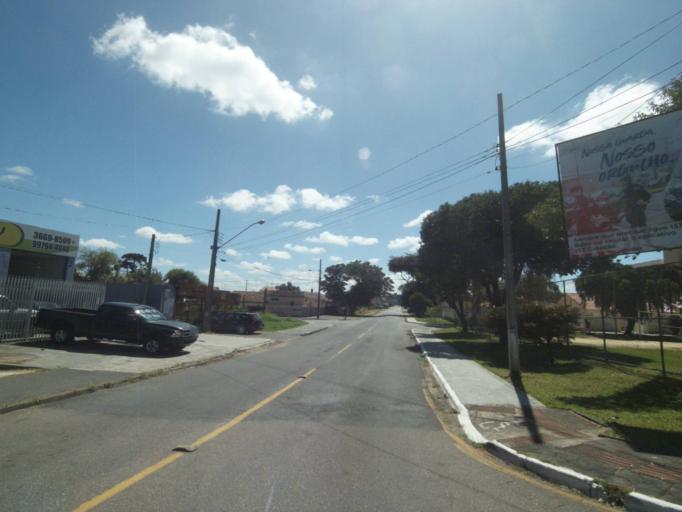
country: BR
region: Parana
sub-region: Pinhais
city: Pinhais
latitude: -25.4430
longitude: -49.1991
